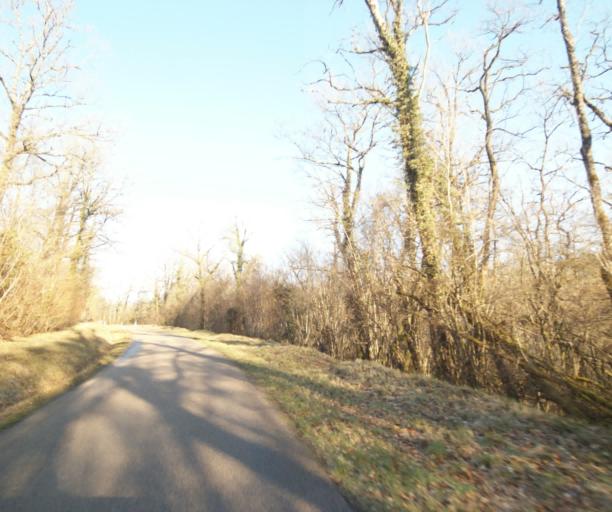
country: FR
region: Champagne-Ardenne
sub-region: Departement de la Haute-Marne
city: Chevillon
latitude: 48.5444
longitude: 5.1225
